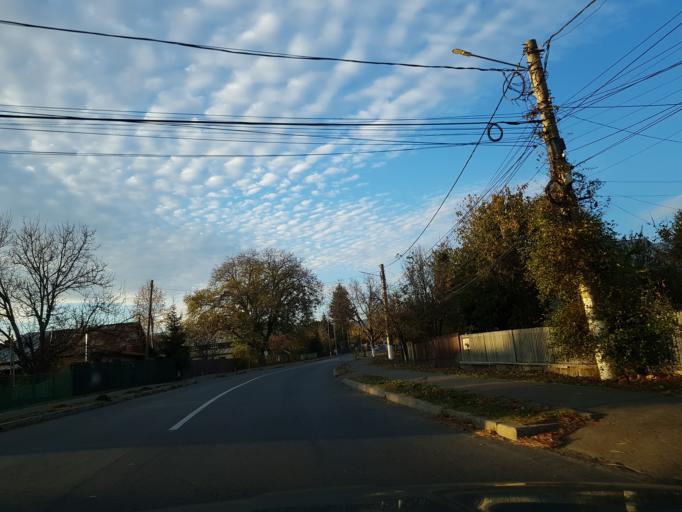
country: RO
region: Prahova
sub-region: Oras Breaza
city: Breaza
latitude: 45.1867
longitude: 25.6624
